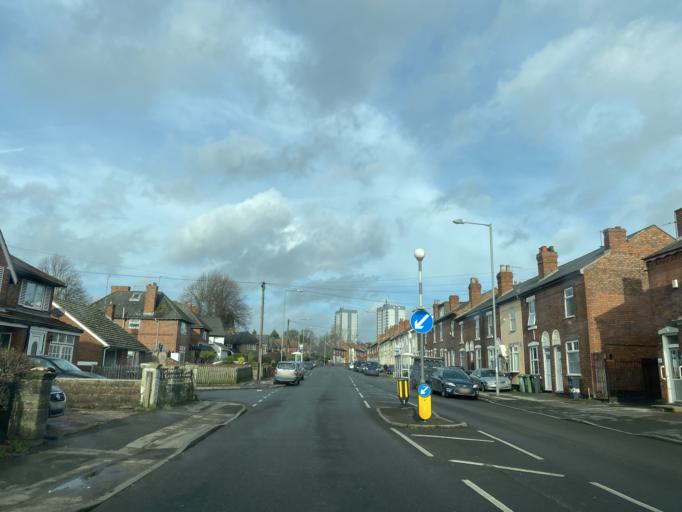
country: GB
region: England
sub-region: Walsall
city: Walsall
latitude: 52.5705
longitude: -1.9804
